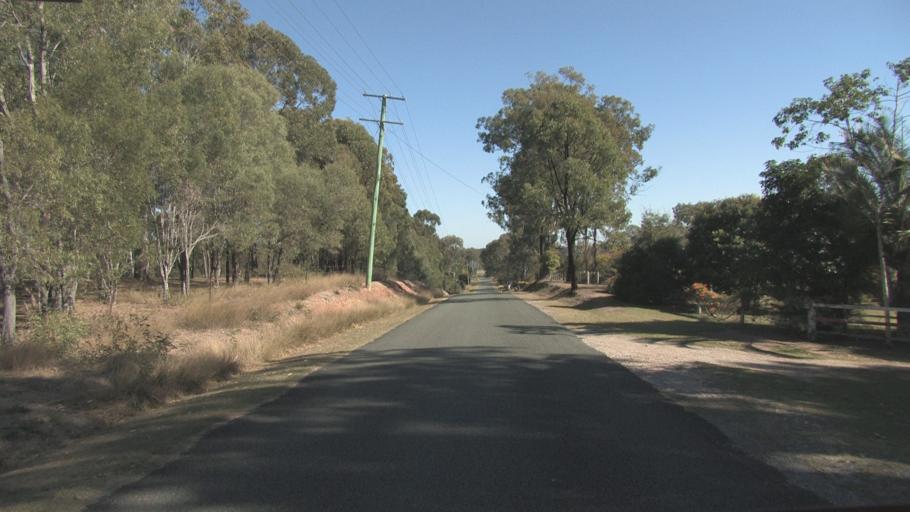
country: AU
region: Queensland
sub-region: Logan
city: Chambers Flat
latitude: -27.7844
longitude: 153.1424
